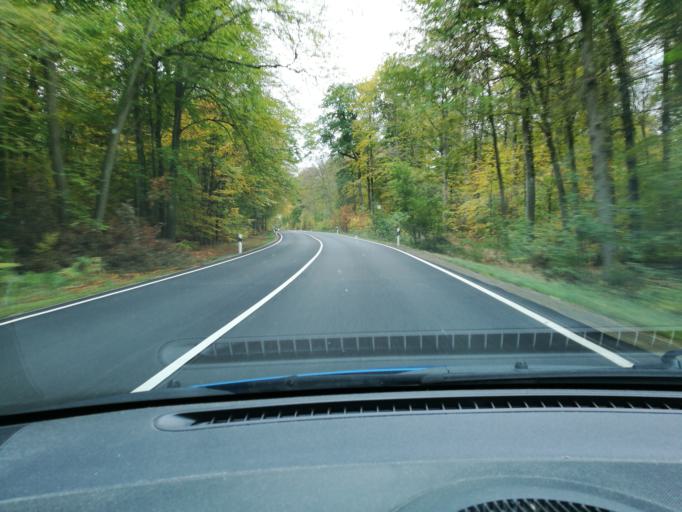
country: DE
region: Schleswig-Holstein
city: Fredeburg
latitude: 53.6665
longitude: 10.7182
